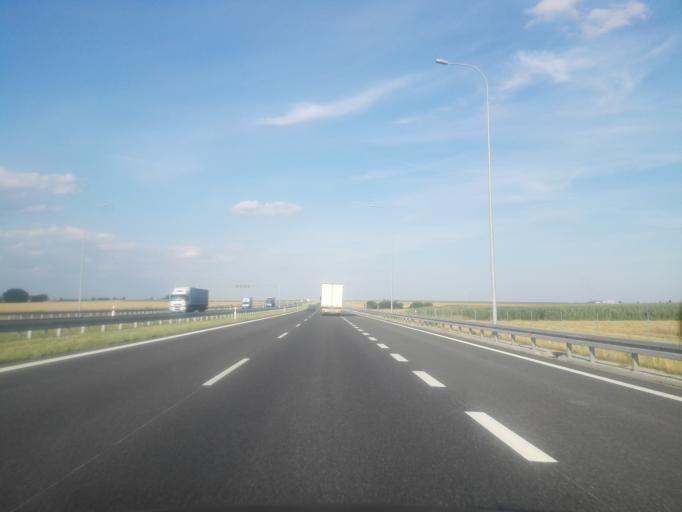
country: PL
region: Greater Poland Voivodeship
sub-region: Powiat kepinski
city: Kepno
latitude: 51.3159
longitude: 18.0196
